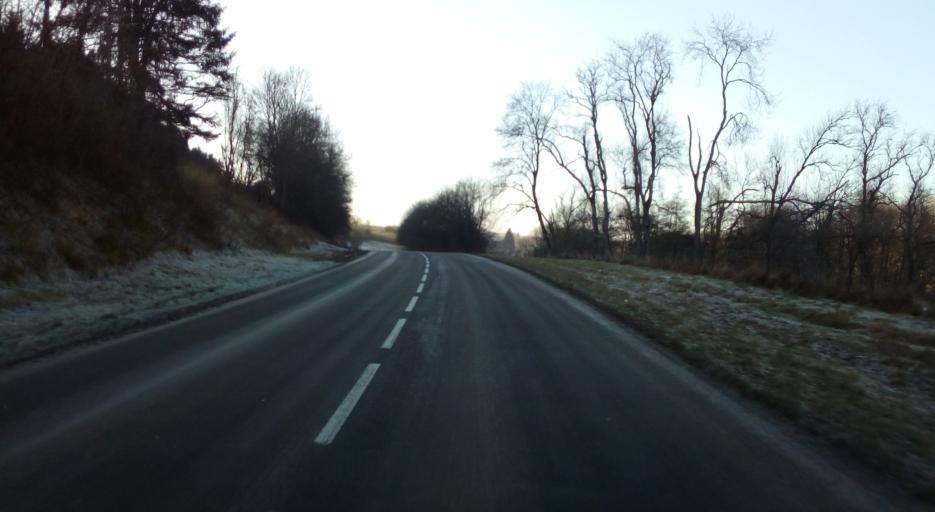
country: FR
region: Champagne-Ardenne
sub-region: Departement des Ardennes
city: Rimogne
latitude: 49.7774
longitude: 4.4117
